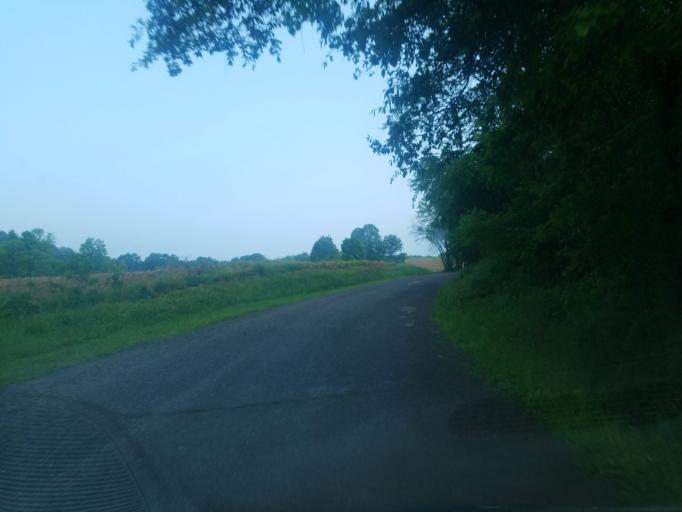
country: US
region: Ohio
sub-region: Stark County
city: Minerva
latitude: 40.7562
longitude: -80.9502
